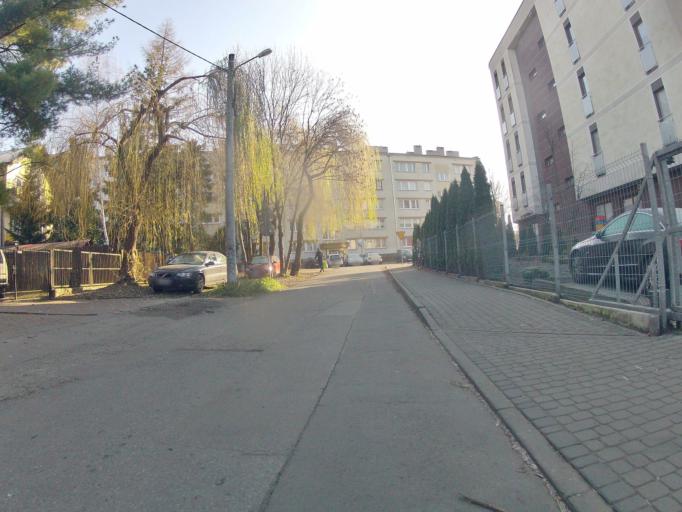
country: PL
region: Lesser Poland Voivodeship
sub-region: Krakow
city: Krakow
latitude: 50.0839
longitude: 19.9590
